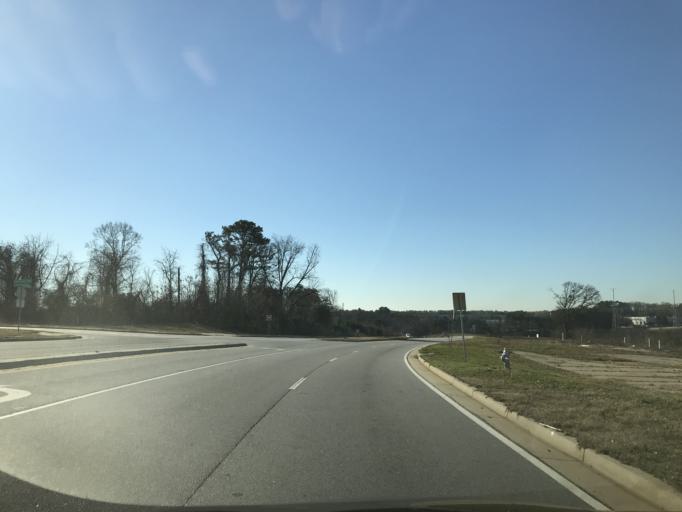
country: US
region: Georgia
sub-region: Fulton County
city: Hapeville
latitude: 33.6222
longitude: -84.4086
